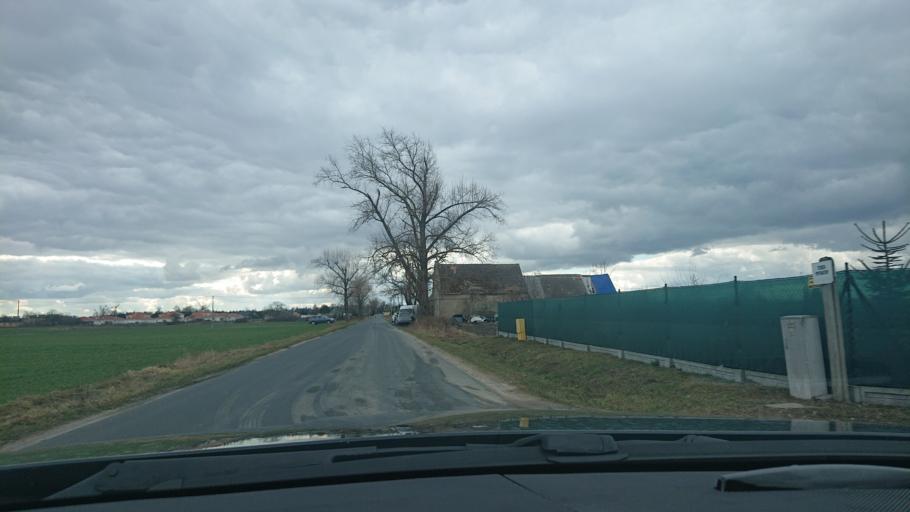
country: PL
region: Greater Poland Voivodeship
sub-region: Powiat gnieznienski
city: Gniezno
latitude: 52.5806
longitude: 17.6407
